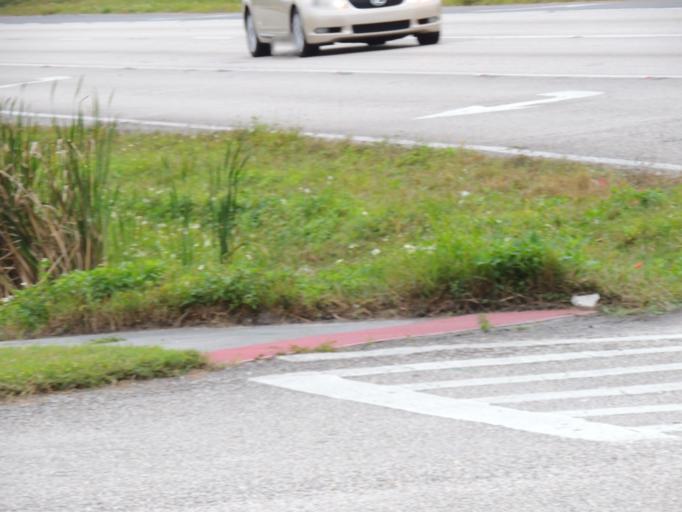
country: US
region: Florida
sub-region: Osceola County
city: Buenaventura Lakes
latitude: 28.2819
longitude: -81.3472
